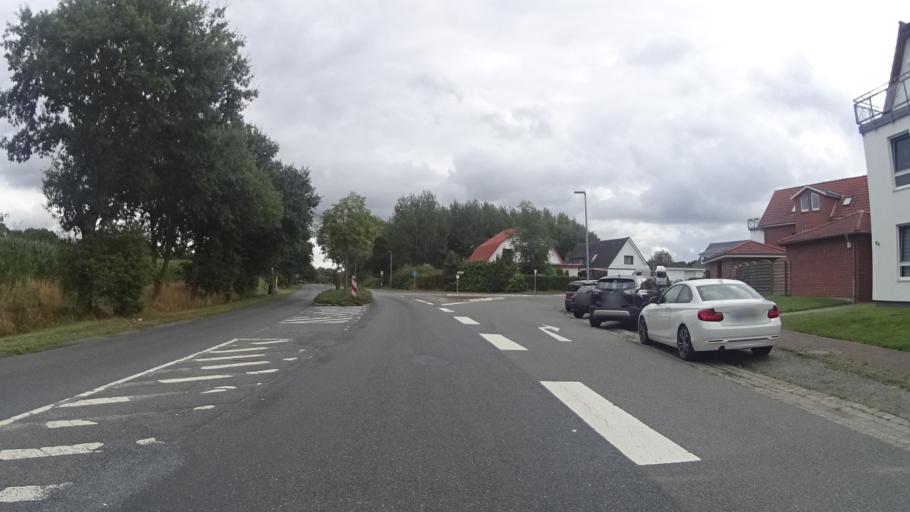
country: DE
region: Lower Saxony
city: Schiffdorf
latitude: 53.5343
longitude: 8.6642
